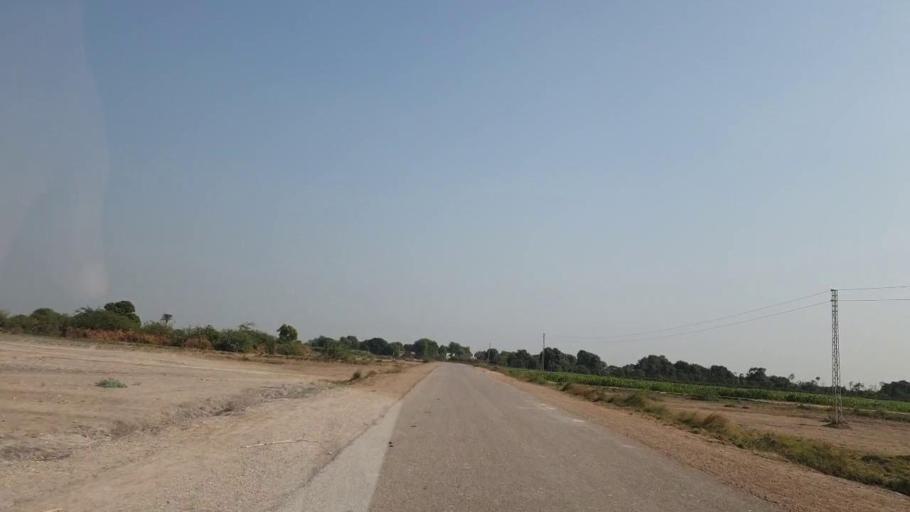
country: PK
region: Sindh
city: Matiari
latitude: 25.5018
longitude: 68.4403
